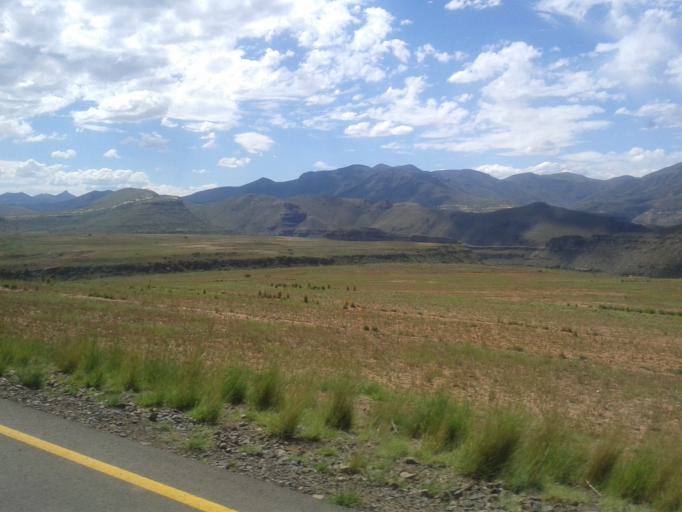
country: LS
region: Qacha's Nek
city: Qacha's Nek
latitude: -30.0377
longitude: 28.3482
